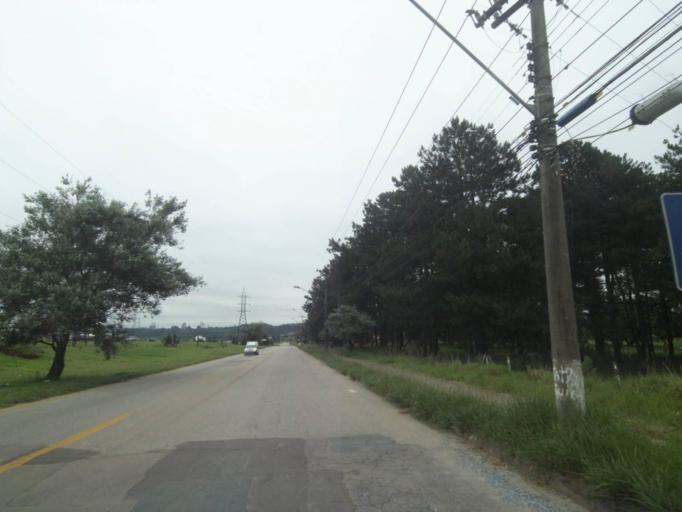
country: BR
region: Parana
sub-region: Araucaria
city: Araucaria
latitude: -25.5508
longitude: -49.3307
